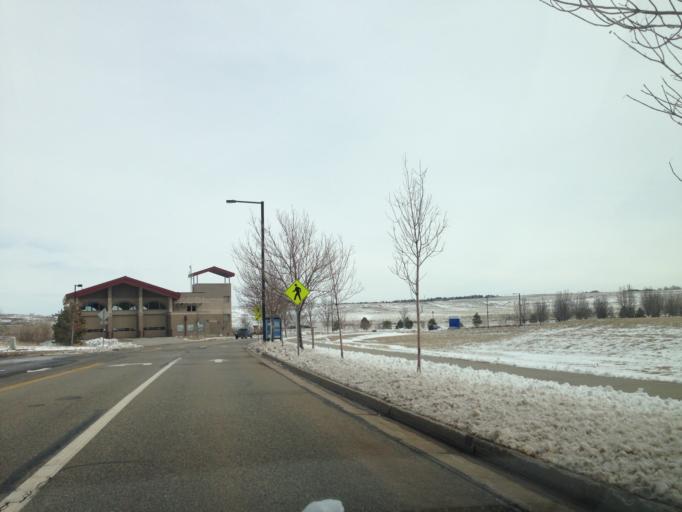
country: US
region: Colorado
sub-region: Boulder County
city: Lafayette
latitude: 39.9721
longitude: -105.0851
